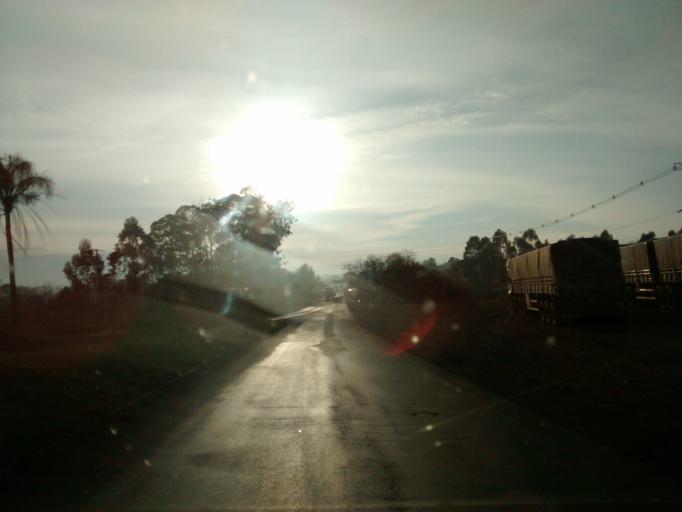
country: BR
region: Parana
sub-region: Francisco Beltrao
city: Francisco Beltrao
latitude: -26.1529
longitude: -53.0220
